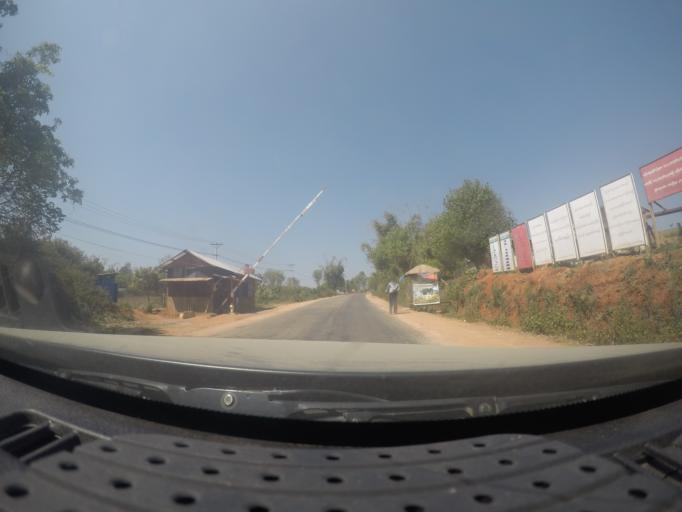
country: MM
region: Shan
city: Taunggyi
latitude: 20.7903
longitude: 96.6410
